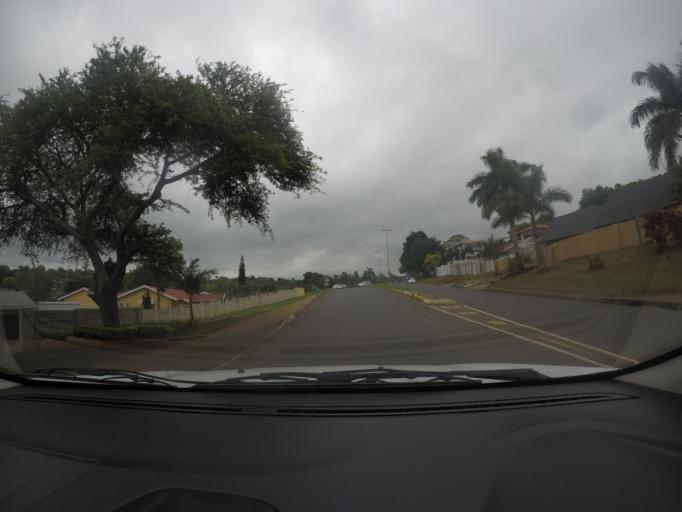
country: ZA
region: KwaZulu-Natal
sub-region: uThungulu District Municipality
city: Empangeni
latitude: -28.7695
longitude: 31.8949
